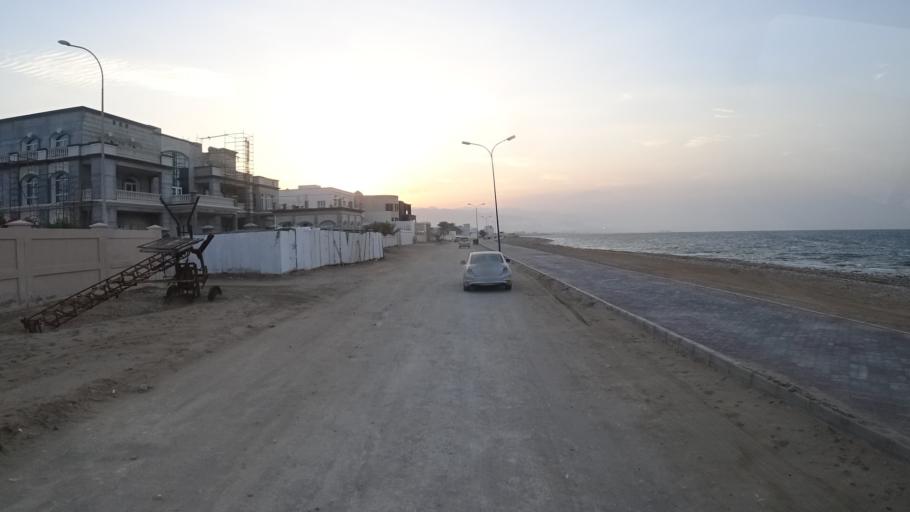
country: OM
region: Ash Sharqiyah
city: Sur
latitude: 22.5924
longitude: 59.5007
